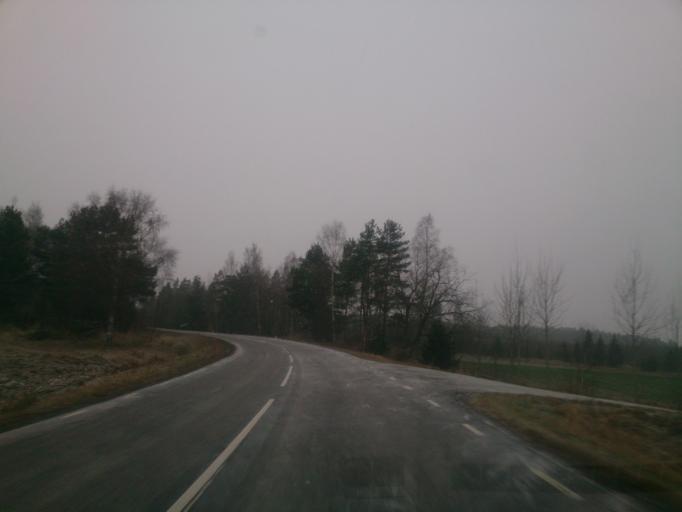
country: SE
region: OEstergoetland
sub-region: Soderkopings Kommun
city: Soederkoeping
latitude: 58.5130
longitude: 16.3366
